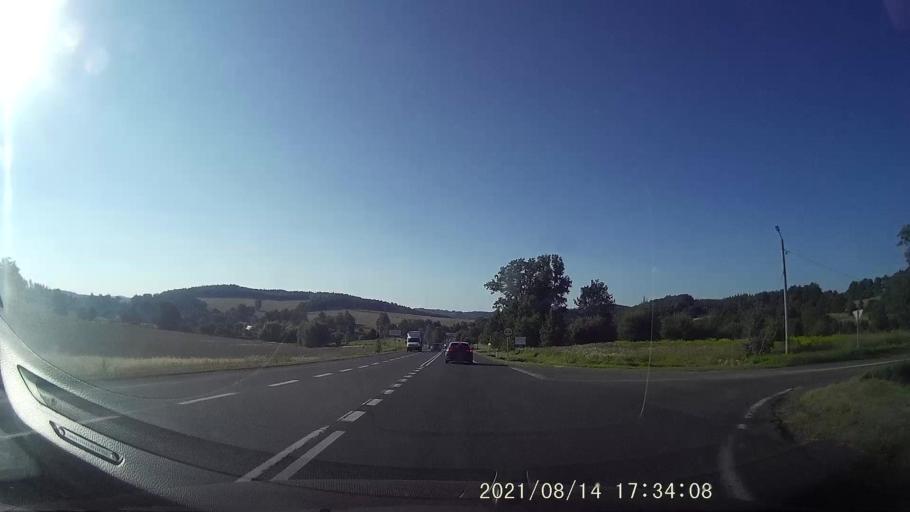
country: PL
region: Lower Silesian Voivodeship
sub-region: Powiat jeleniogorski
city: Stara Kamienica
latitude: 50.9335
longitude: 15.6019
